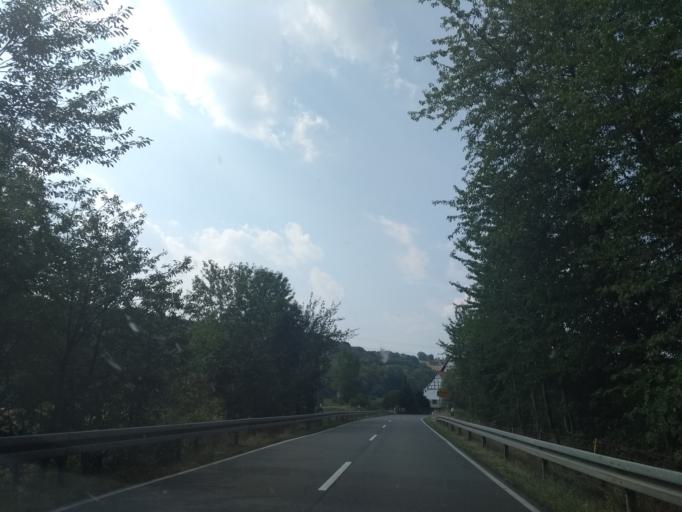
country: DE
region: Saxony-Anhalt
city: Droyssig
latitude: 51.0241
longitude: 12.0481
